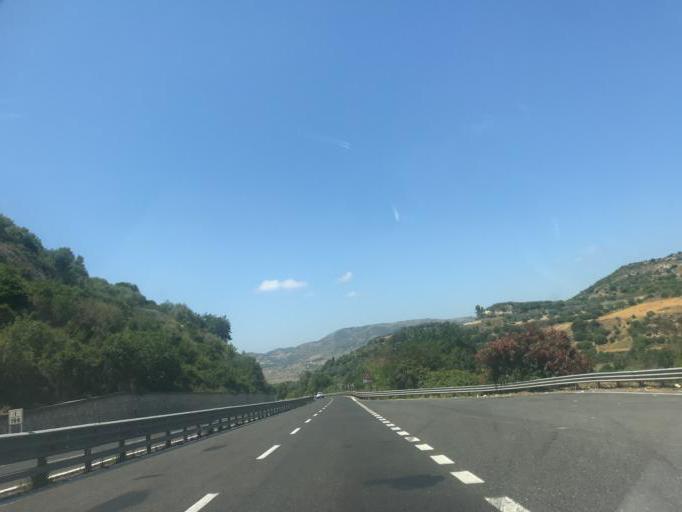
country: IT
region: Sardinia
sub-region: Provincia di Sassari
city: Codrongianos
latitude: 40.6572
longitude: 8.6716
